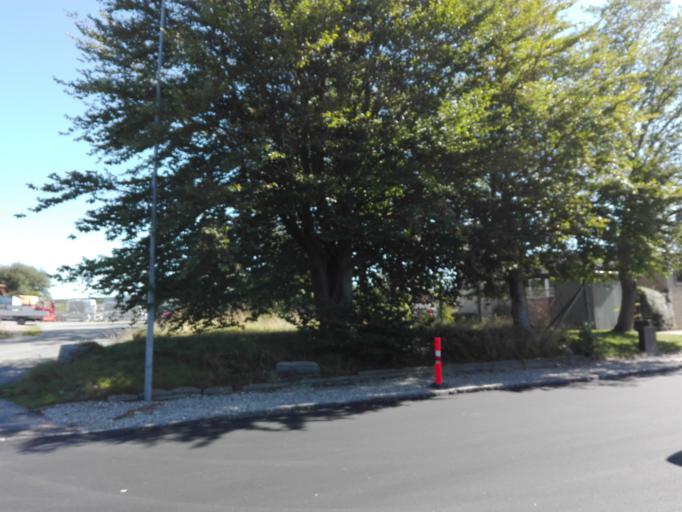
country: DK
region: Central Jutland
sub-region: Arhus Kommune
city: Tranbjerg
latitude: 56.1061
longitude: 10.1512
